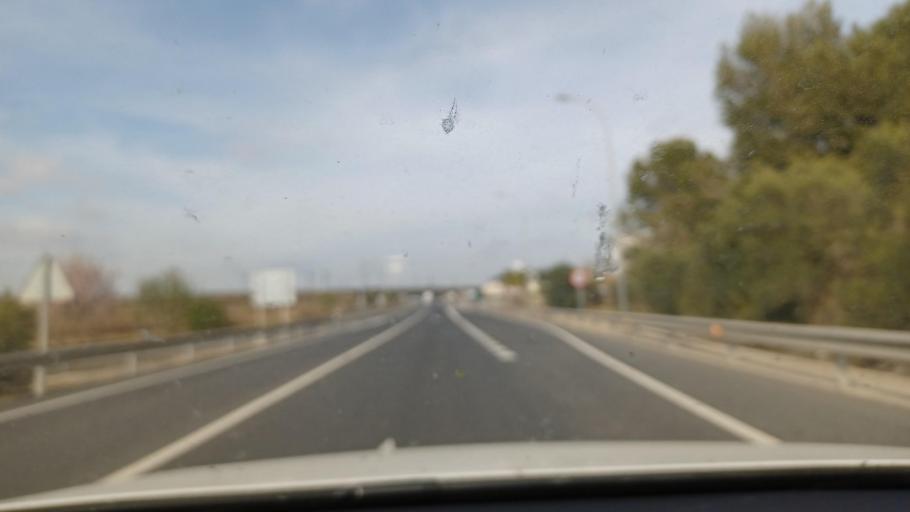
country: ES
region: Catalonia
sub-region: Provincia de Tarragona
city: la Pobla de Mafumet
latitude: 41.1874
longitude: 1.2423
